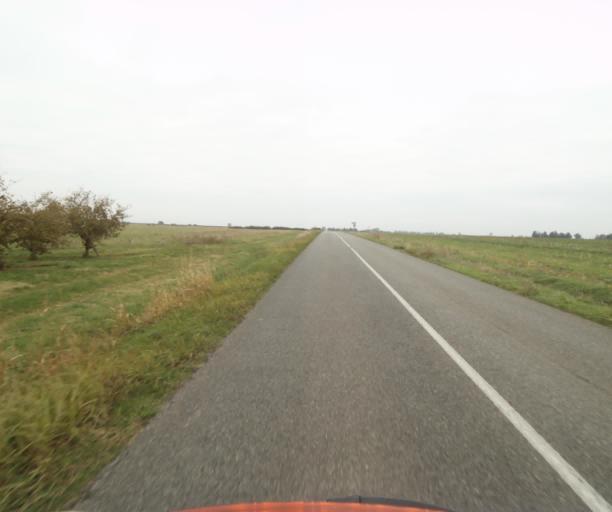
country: FR
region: Midi-Pyrenees
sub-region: Departement du Tarn-et-Garonne
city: Verdun-sur-Garonne
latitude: 43.8173
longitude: 1.1895
